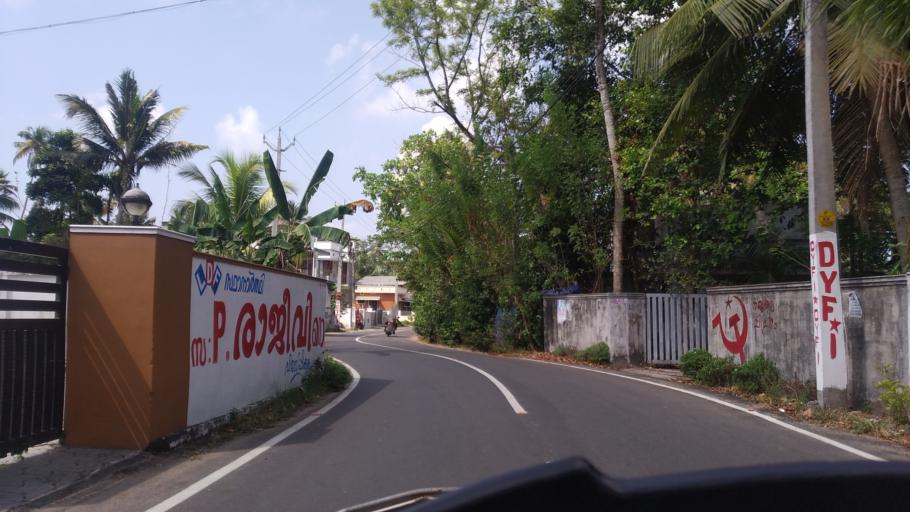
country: IN
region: Kerala
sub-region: Ernakulam
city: Elur
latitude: 10.1154
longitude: 76.2373
